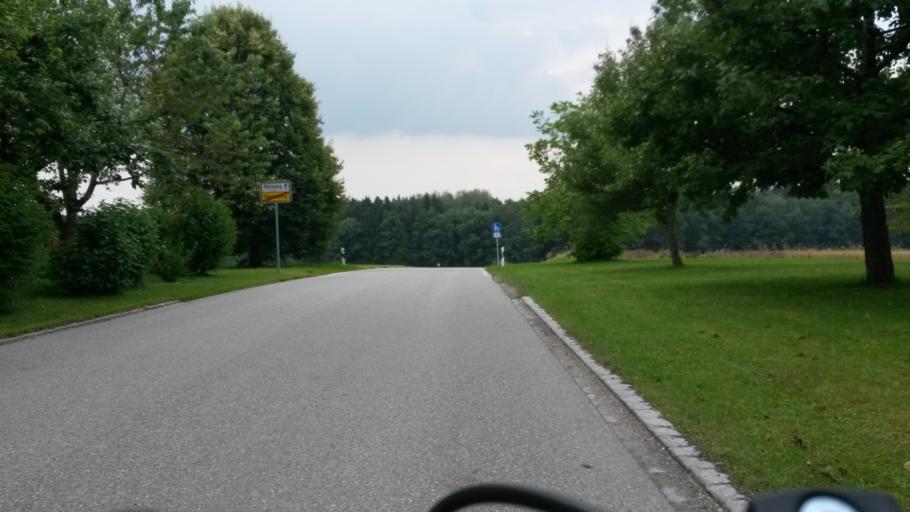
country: DE
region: Bavaria
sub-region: Upper Bavaria
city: Amerang
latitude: 47.9756
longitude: 12.3095
